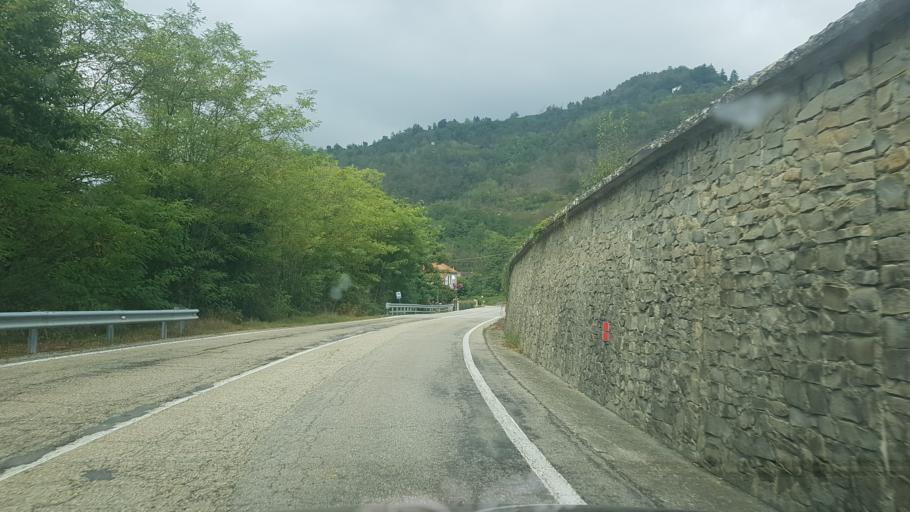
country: IT
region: Piedmont
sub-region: Provincia di Cuneo
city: Monesiglio
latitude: 44.4812
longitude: 8.1147
